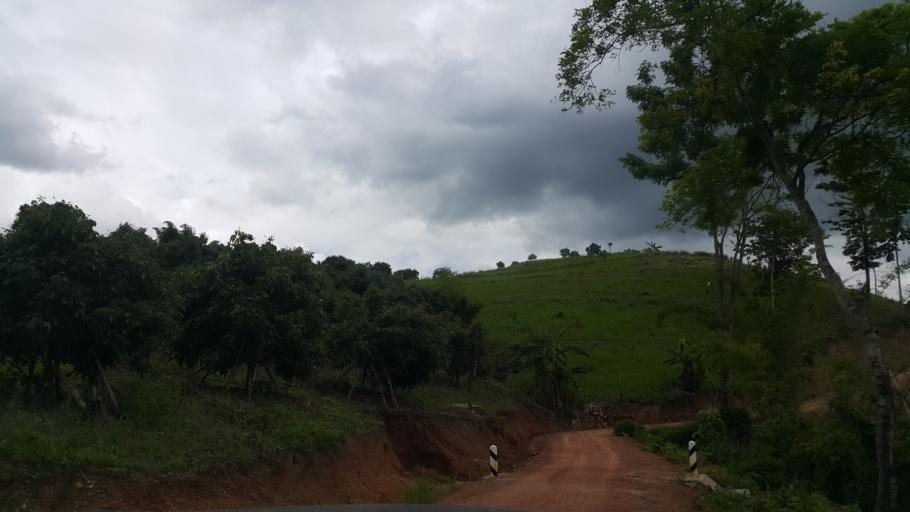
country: TH
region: Chiang Mai
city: Mae Taeng
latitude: 19.2182
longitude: 98.9980
